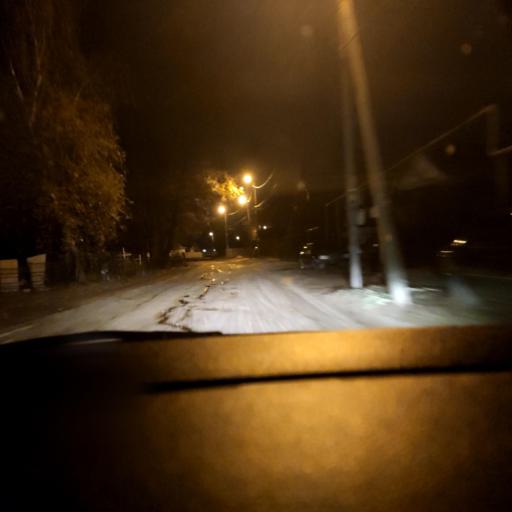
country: RU
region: Voronezj
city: Podgornoye
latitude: 51.7312
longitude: 39.1459
